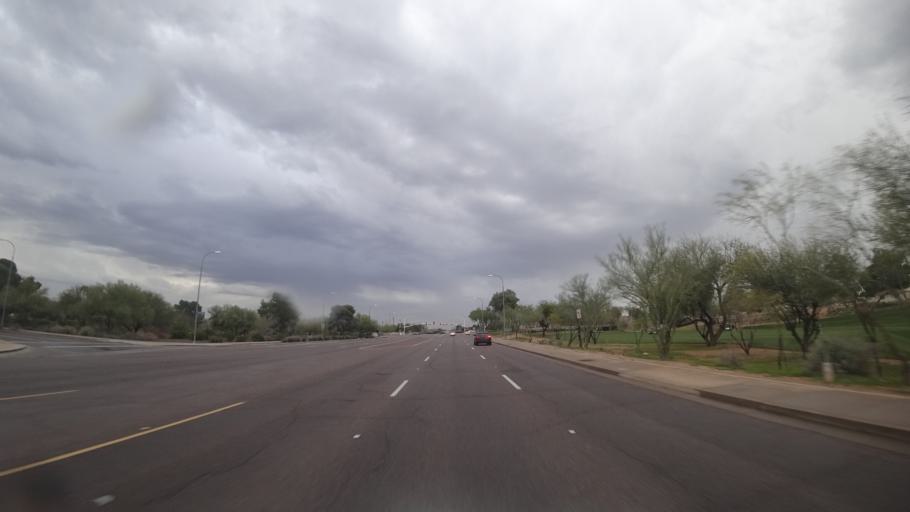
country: US
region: Arizona
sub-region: Maricopa County
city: Scottsdale
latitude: 33.5260
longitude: -111.9089
